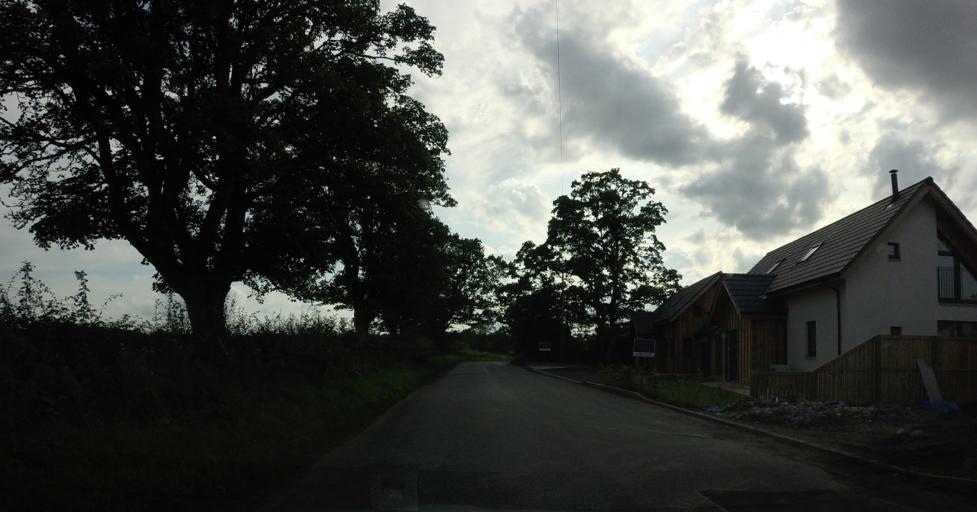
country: GB
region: Scotland
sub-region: Perth and Kinross
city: Auchterarder
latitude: 56.3052
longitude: -3.7433
